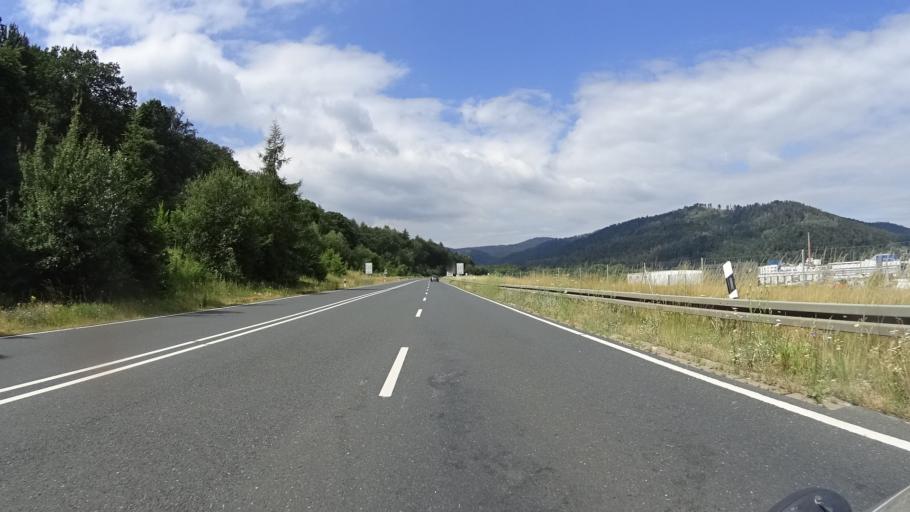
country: DE
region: Lower Saxony
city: Langelsheim
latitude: 51.9290
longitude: 10.3337
